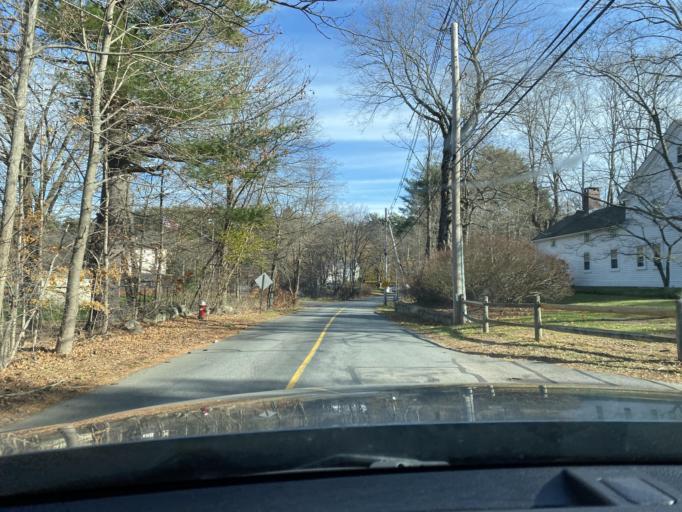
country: US
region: Massachusetts
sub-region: Norfolk County
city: Medfield
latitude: 42.1831
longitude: -71.2967
